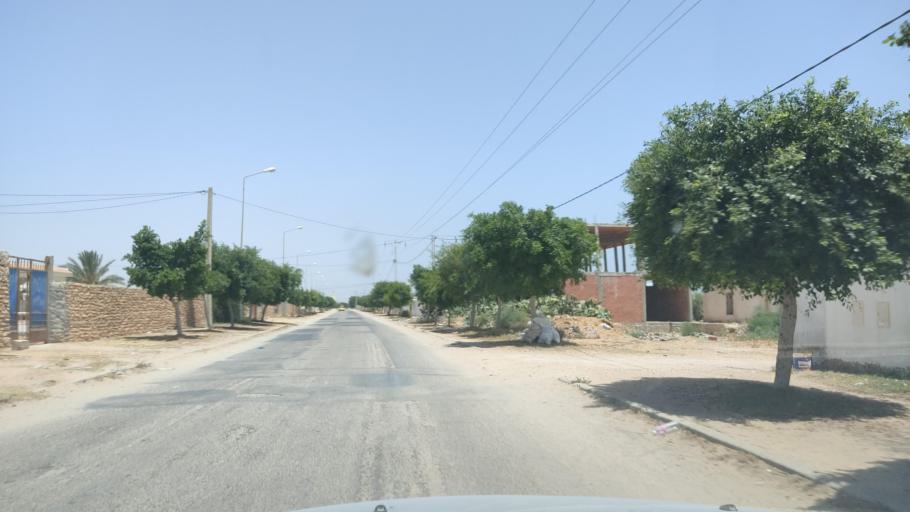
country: TN
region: Safaqis
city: Sfax
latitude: 34.6672
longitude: 10.7106
